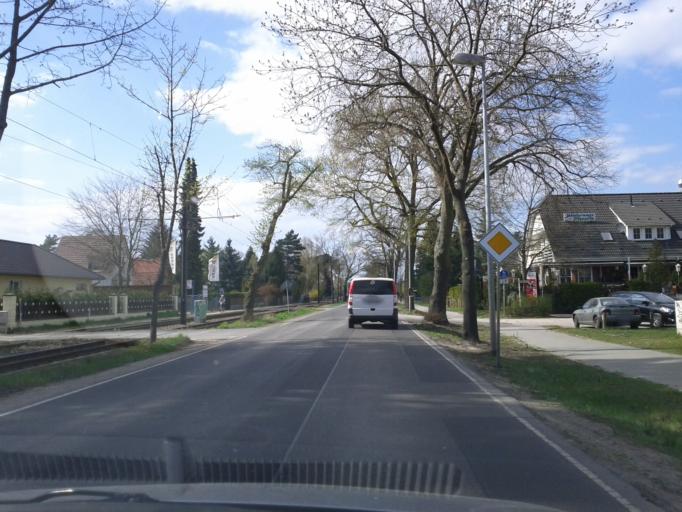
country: DE
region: Brandenburg
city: Schoneiche
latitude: 52.4751
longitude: 13.7120
